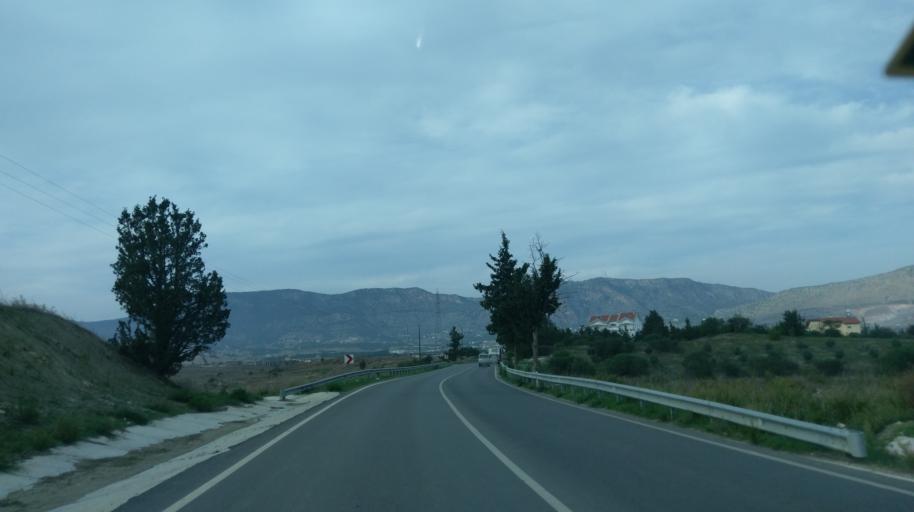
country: CY
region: Keryneia
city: Kyrenia
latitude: 35.2555
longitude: 33.2856
